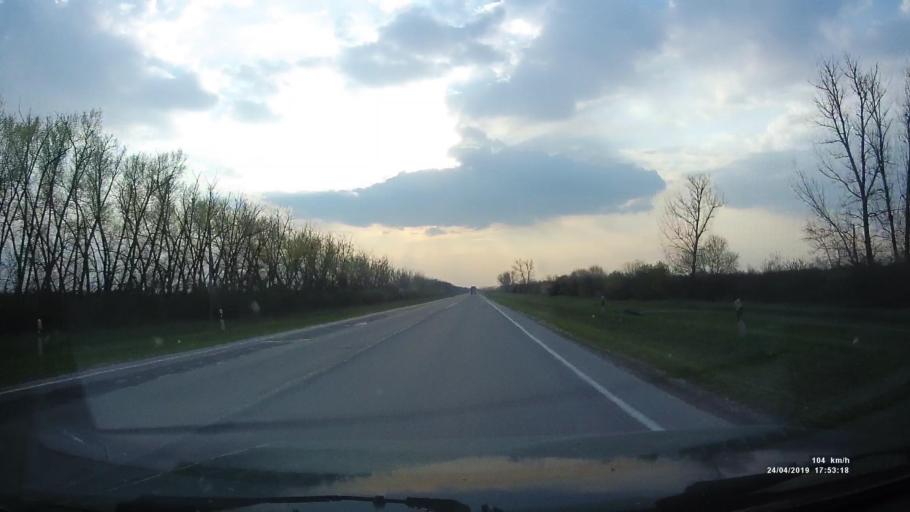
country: RU
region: Rostov
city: Yegorlykskaya
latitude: 46.5516
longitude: 40.7168
